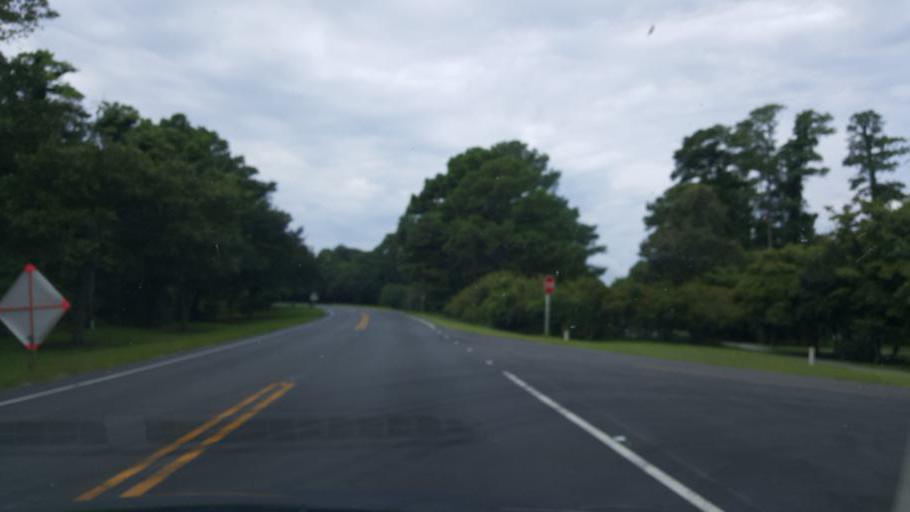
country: US
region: North Carolina
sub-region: Dare County
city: Manteo
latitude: 35.9340
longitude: -75.7005
